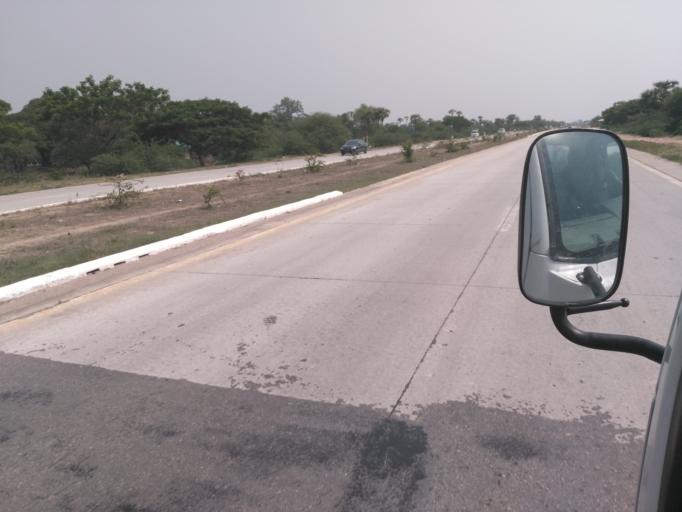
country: MM
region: Sagain
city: Sagaing
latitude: 21.8059
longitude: 95.9739
